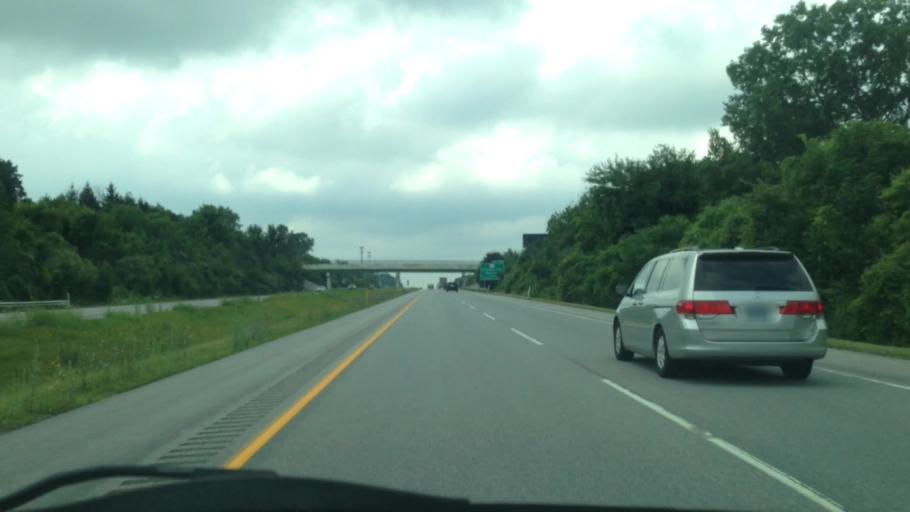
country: US
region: Indiana
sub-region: LaPorte County
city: Westville
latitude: 41.5944
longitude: -86.8752
